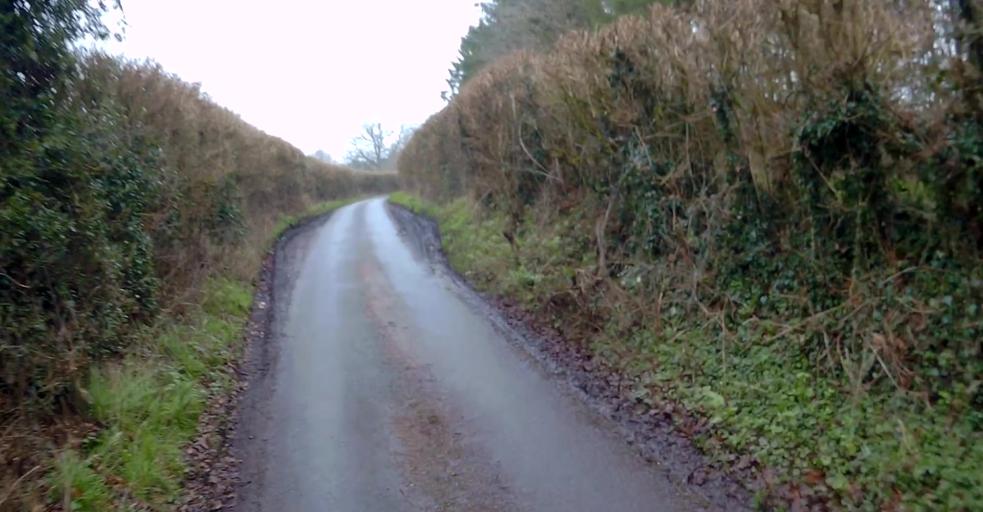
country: GB
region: England
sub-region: Hampshire
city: Eversley
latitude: 51.3392
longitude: -0.9225
